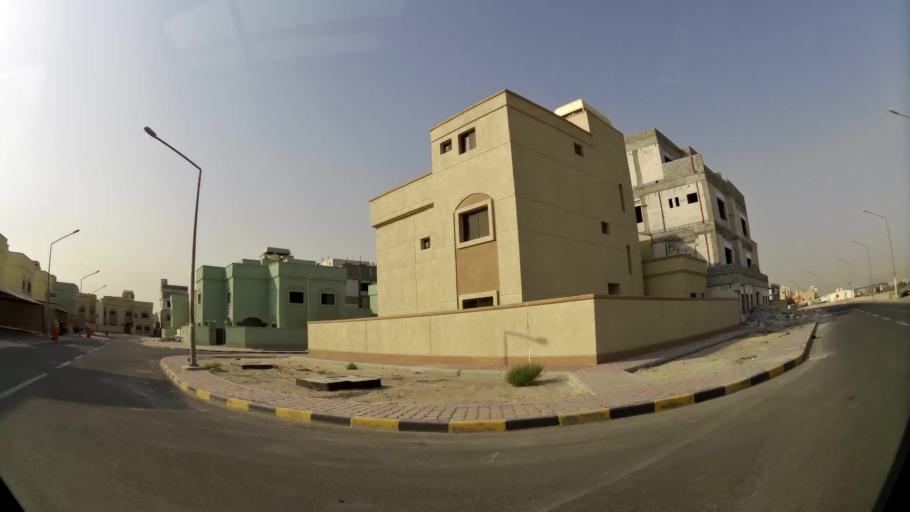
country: KW
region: Al Asimah
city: Ar Rabiyah
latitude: 29.3348
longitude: 47.8081
